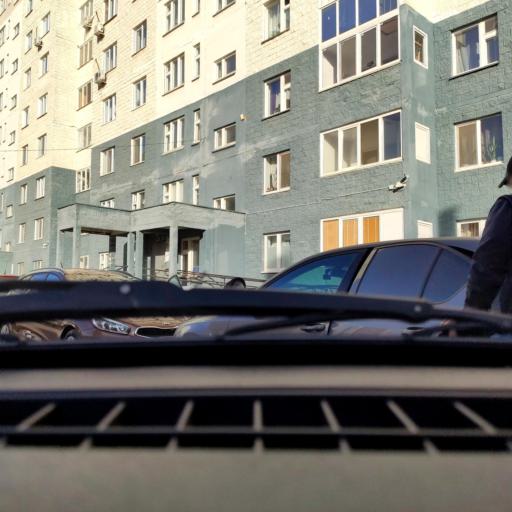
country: RU
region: Bashkortostan
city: Ufa
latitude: 54.7815
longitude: 56.1376
